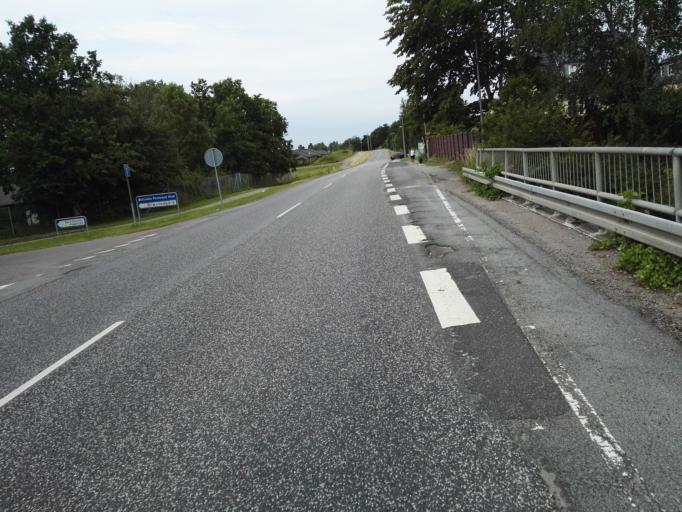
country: DK
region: Capital Region
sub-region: Egedal Kommune
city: Olstykke
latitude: 55.7865
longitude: 12.1462
